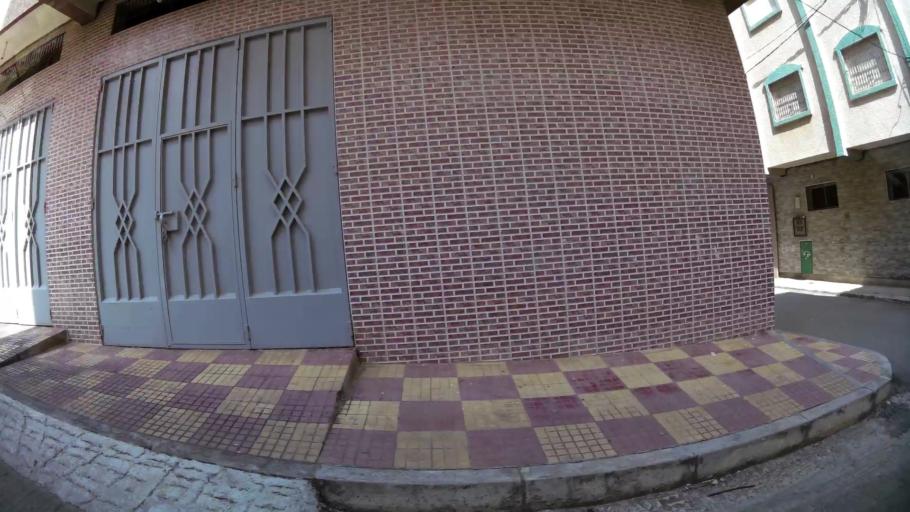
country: MA
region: Tanger-Tetouan
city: Tetouan
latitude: 35.5849
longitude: -5.3559
